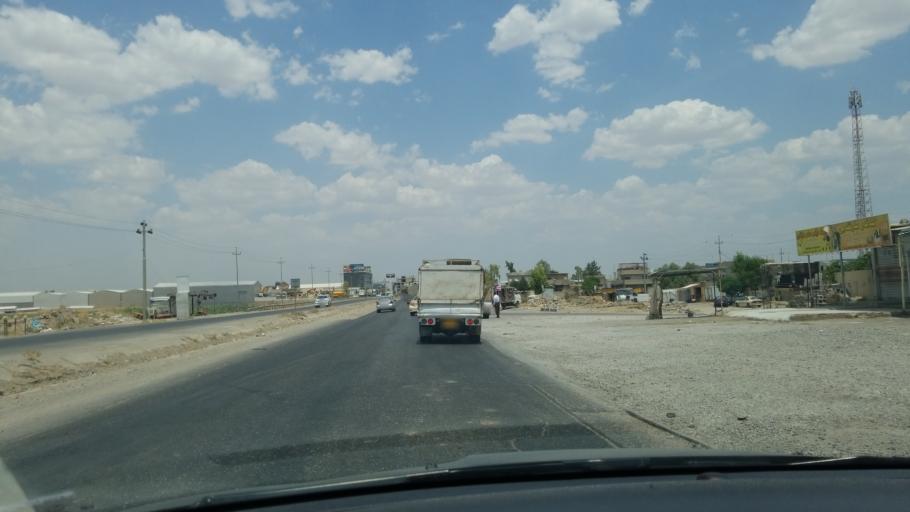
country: IQ
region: Arbil
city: Erbil
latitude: 36.0965
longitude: 44.0216
